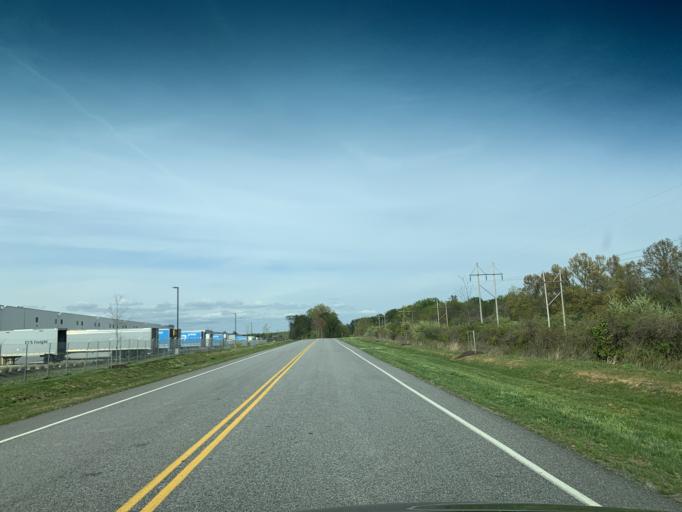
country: US
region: Maryland
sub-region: Harford County
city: Perryman
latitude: 39.4789
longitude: -76.1826
